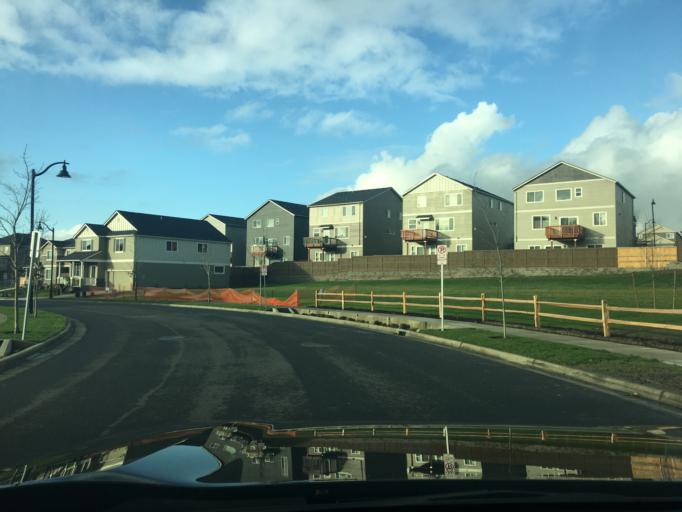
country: US
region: Oregon
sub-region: Washington County
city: Bethany
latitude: 45.5721
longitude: -122.8522
